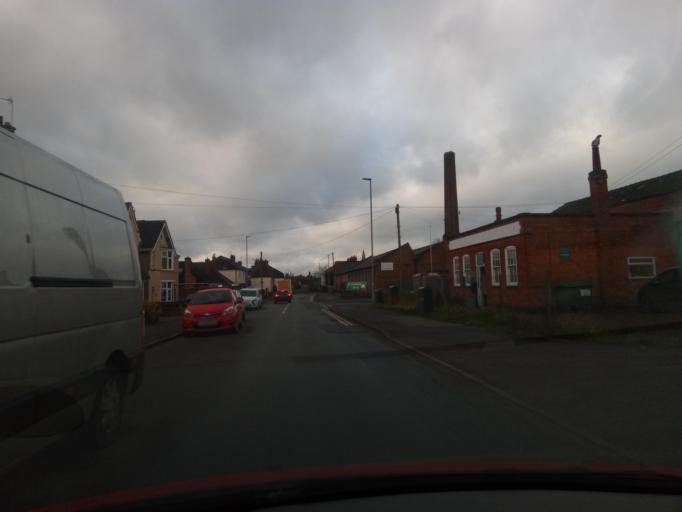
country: GB
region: England
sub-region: Leicestershire
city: Sileby
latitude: 52.7346
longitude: -1.1066
